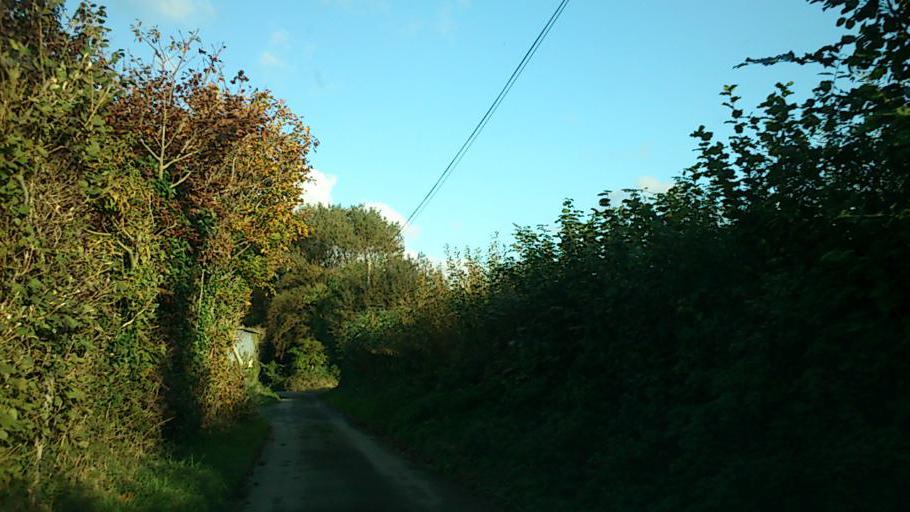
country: GB
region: Wales
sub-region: County of Ceredigion
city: Bow Street
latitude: 52.4566
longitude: -3.9978
